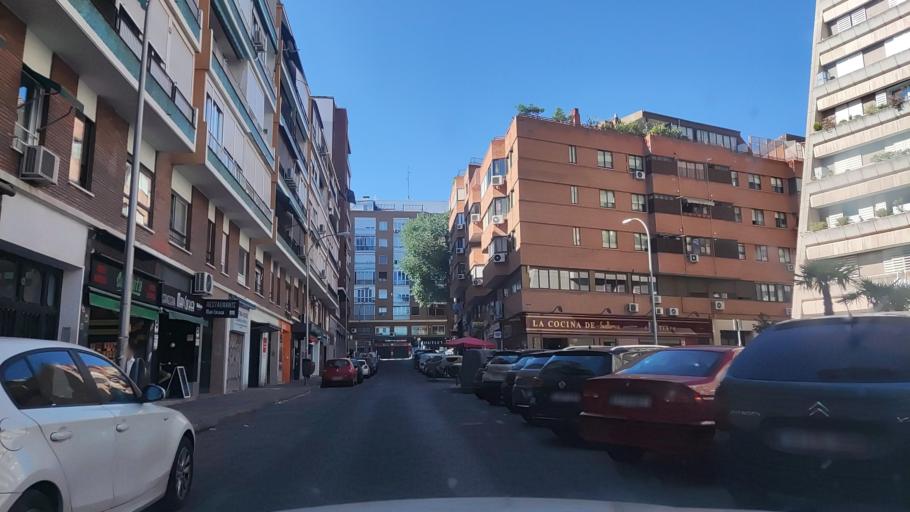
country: ES
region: Madrid
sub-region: Provincia de Madrid
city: Chamartin
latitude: 40.4567
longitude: -3.6780
